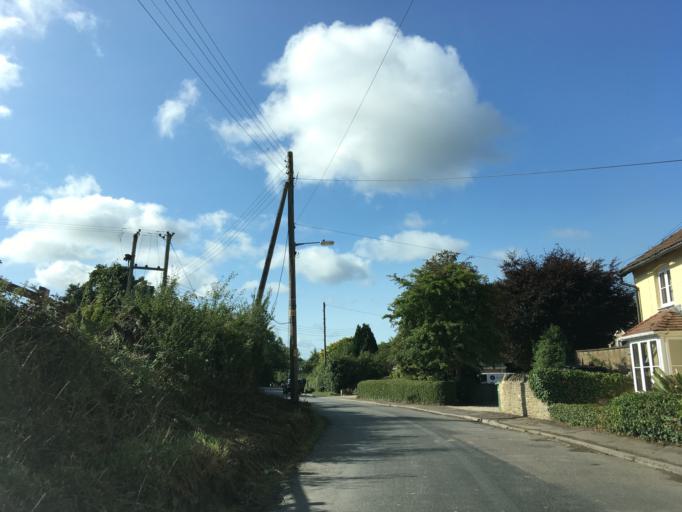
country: GB
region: England
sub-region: South Gloucestershire
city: Horton
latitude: 51.5298
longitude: -2.3587
